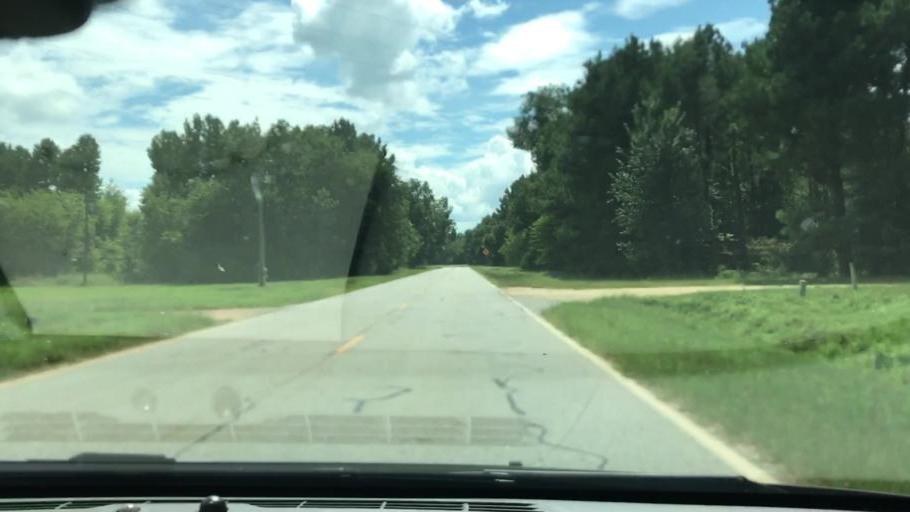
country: US
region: Georgia
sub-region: Quitman County
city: Georgetown
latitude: 32.0502
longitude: -85.0365
